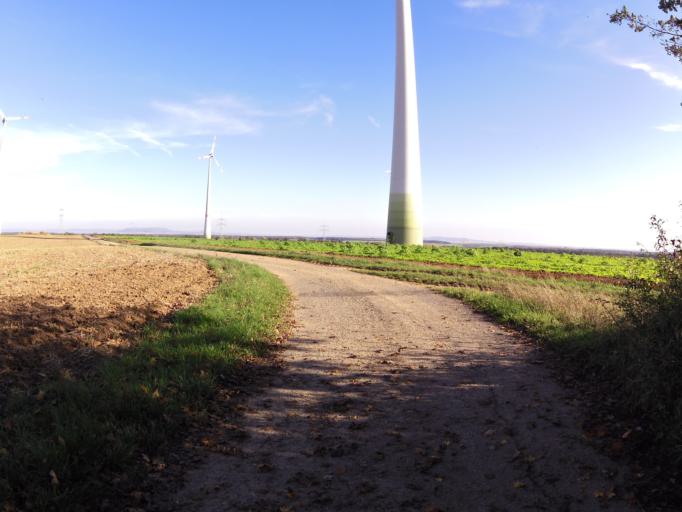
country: DE
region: Bavaria
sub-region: Regierungsbezirk Unterfranken
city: Sommerhausen
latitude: 49.7179
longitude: 10.0427
